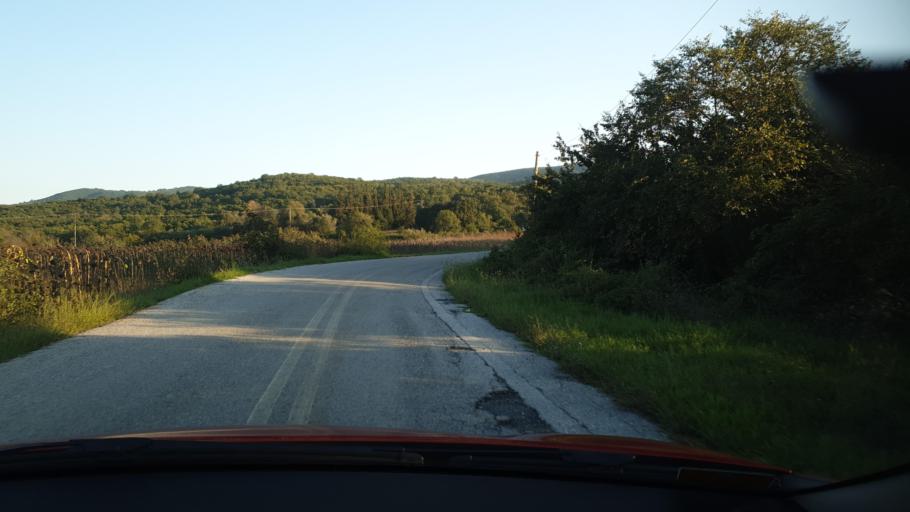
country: GR
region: Central Macedonia
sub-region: Nomos Thessalonikis
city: Gerakarou
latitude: 40.5628
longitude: 23.2820
